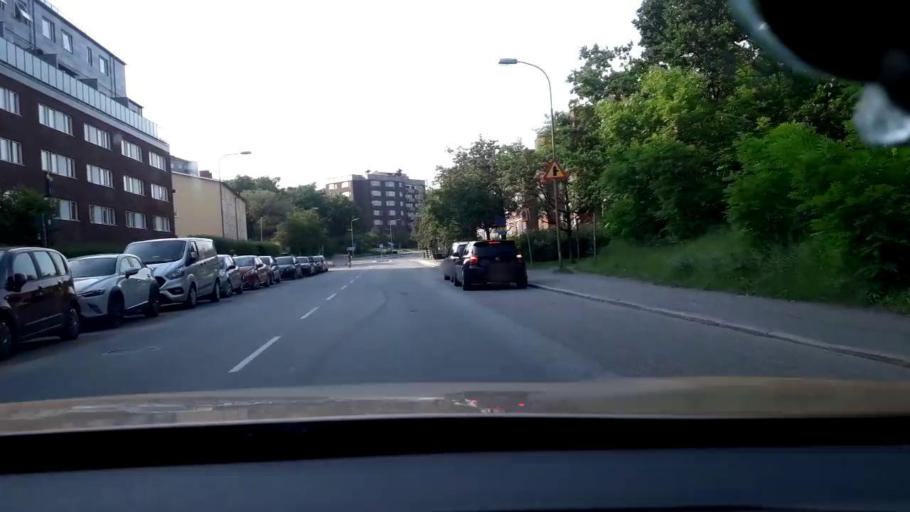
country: SE
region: Stockholm
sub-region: Nacka Kommun
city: Nacka
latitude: 59.3123
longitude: 18.2000
